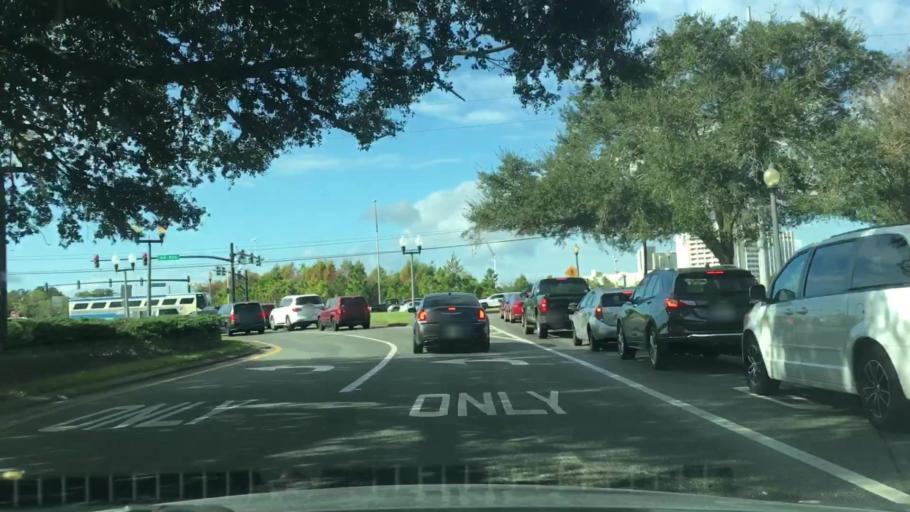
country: US
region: Florida
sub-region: Osceola County
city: Celebration
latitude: 28.3745
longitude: -81.5030
